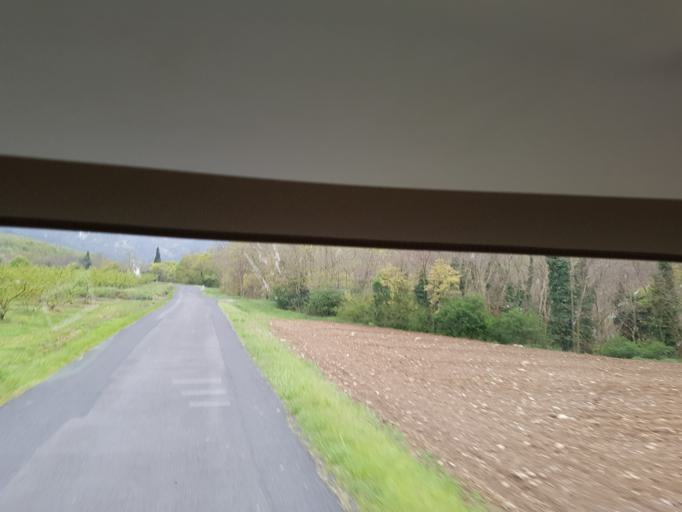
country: FR
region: Languedoc-Roussillon
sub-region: Departement des Pyrenees-Orientales
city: Prades
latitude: 42.5929
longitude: 2.4183
